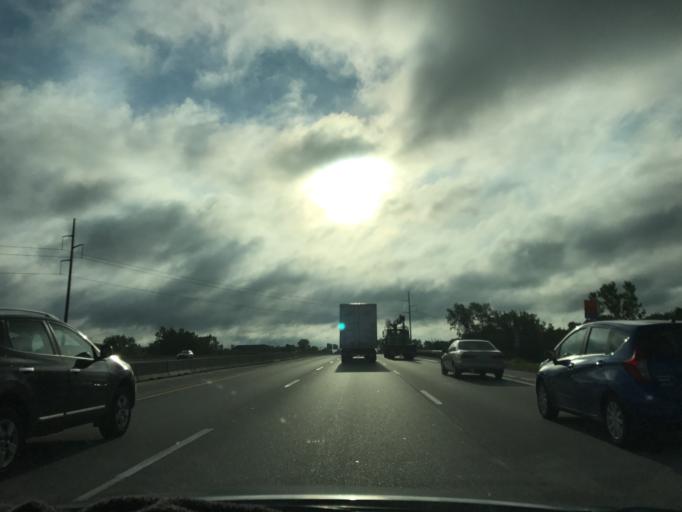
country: US
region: Iowa
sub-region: Johnson County
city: Tiffin
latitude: 41.6942
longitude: -91.6228
